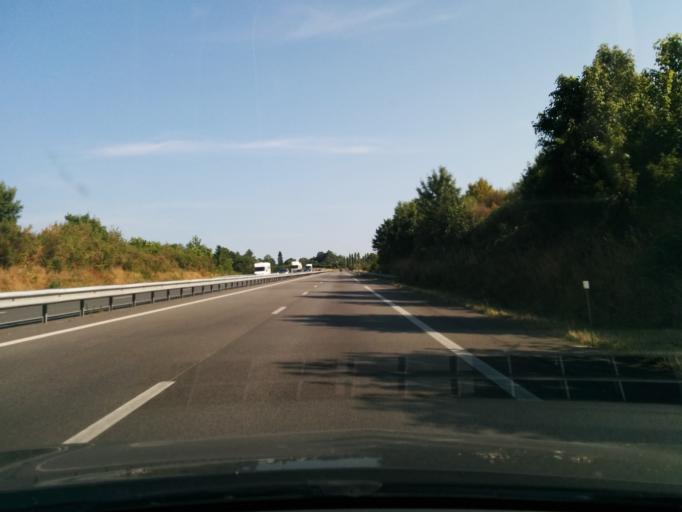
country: FR
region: Limousin
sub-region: Departement de la Haute-Vienne
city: Vicq-sur-Breuilh
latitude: 45.6533
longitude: 1.4033
